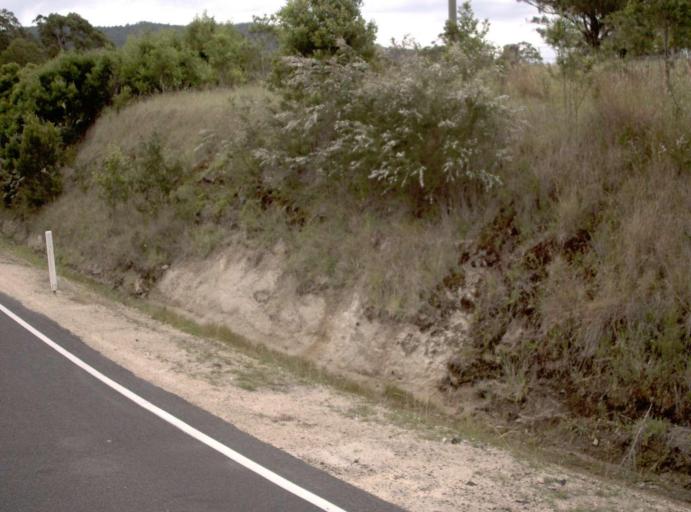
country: AU
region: New South Wales
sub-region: Bombala
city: Bombala
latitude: -37.4743
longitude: 149.1768
